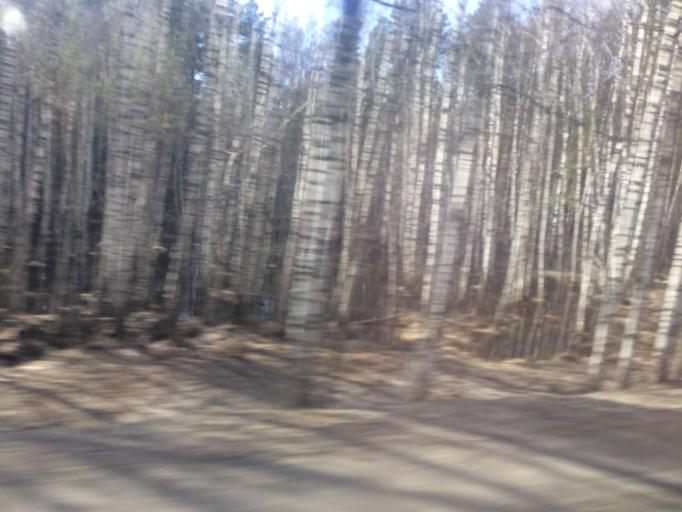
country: RU
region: Tatarstan
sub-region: Zelenodol'skiy Rayon
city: Vasil'yevo
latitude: 55.8928
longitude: 48.7280
